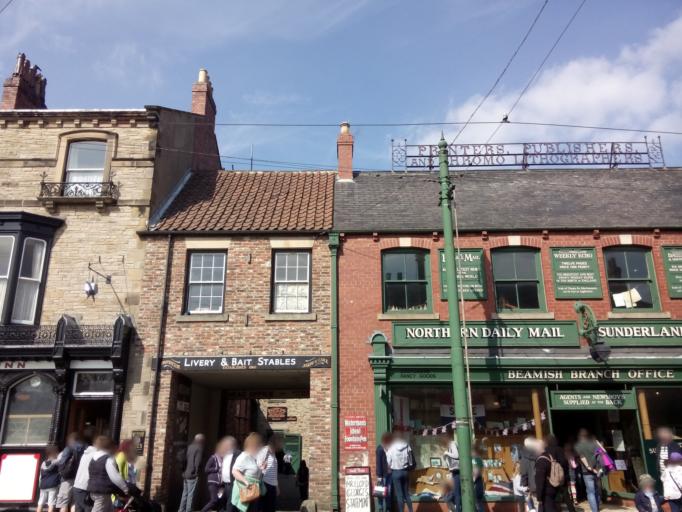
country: GB
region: England
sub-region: County Durham
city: Stanley
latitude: 54.8892
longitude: -1.6610
